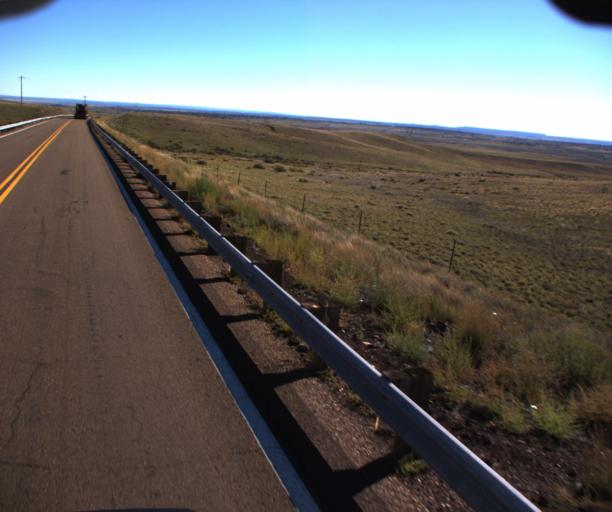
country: US
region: Arizona
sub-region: Apache County
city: Saint Johns
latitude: 34.5067
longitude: -109.4773
